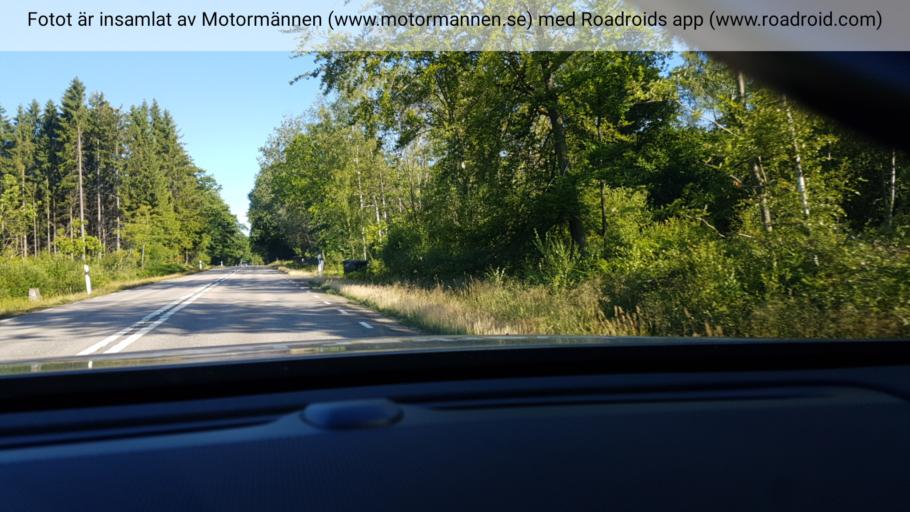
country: SE
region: Kronoberg
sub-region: Markaryds Kommun
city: Markaryd
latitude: 56.4128
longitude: 13.6352
